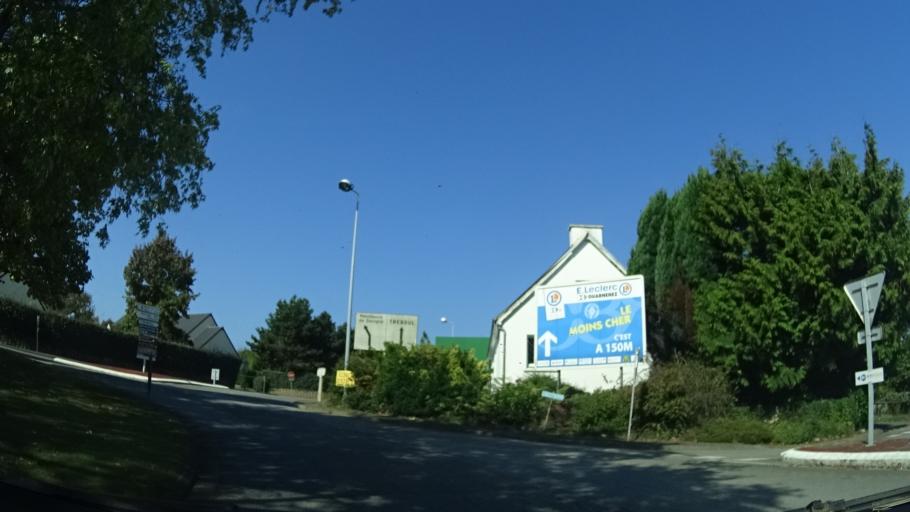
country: FR
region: Brittany
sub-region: Departement du Finistere
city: Douarnenez
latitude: 48.0863
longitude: -4.3462
